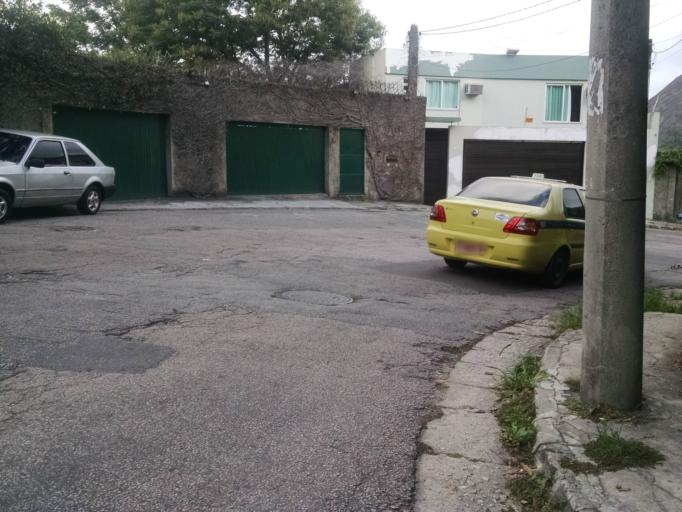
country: BR
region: Rio de Janeiro
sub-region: Rio De Janeiro
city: Rio de Janeiro
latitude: -22.9363
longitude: -43.1963
